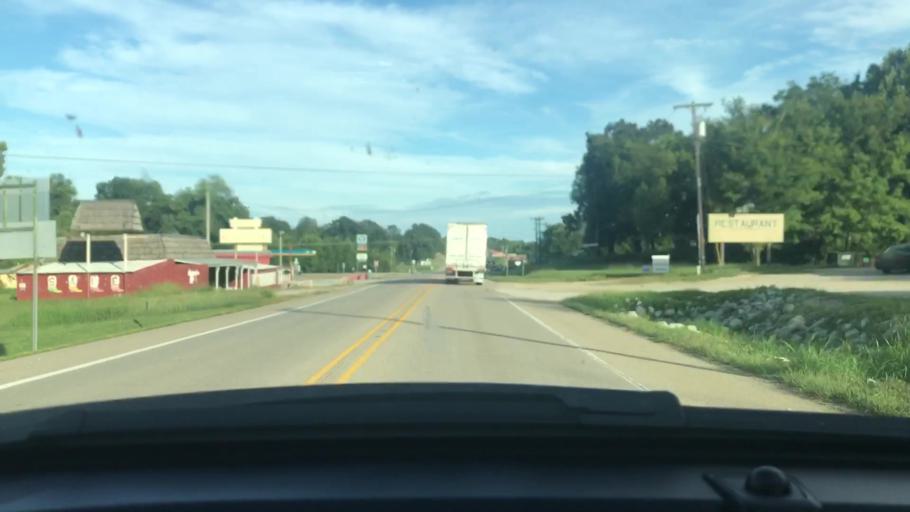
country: US
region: Arkansas
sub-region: Sharp County
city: Cherokee Village
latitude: 36.2372
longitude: -91.2544
